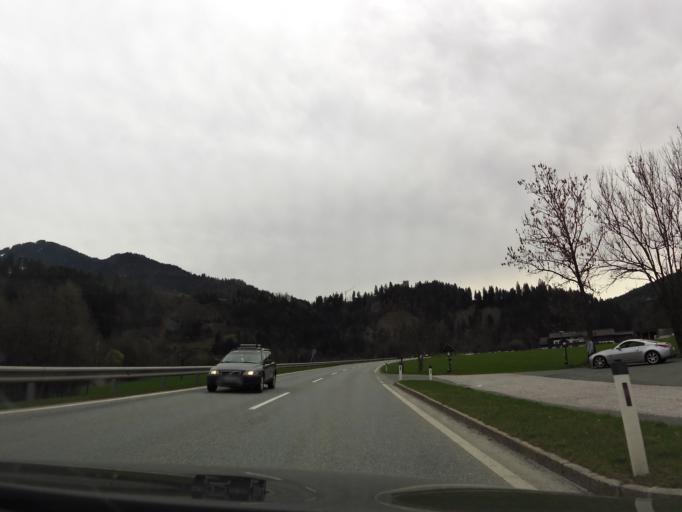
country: AT
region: Tyrol
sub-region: Politischer Bezirk Kitzbuhel
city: Itter
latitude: 47.4780
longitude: 12.1329
